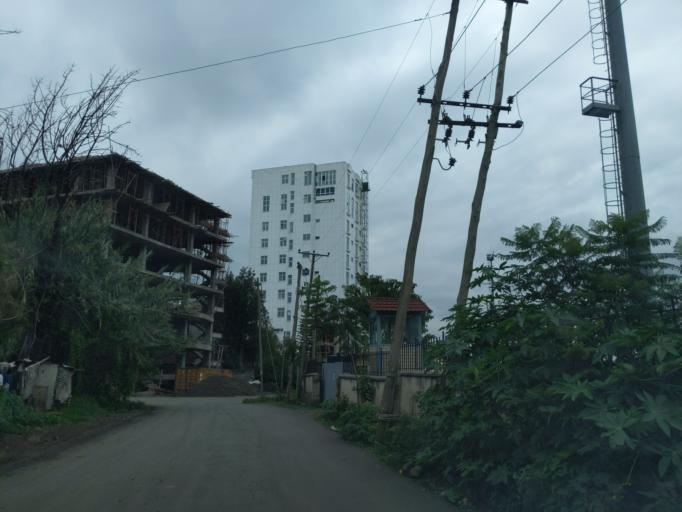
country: ET
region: Adis Abeba
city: Addis Ababa
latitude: 8.9919
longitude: 38.7894
